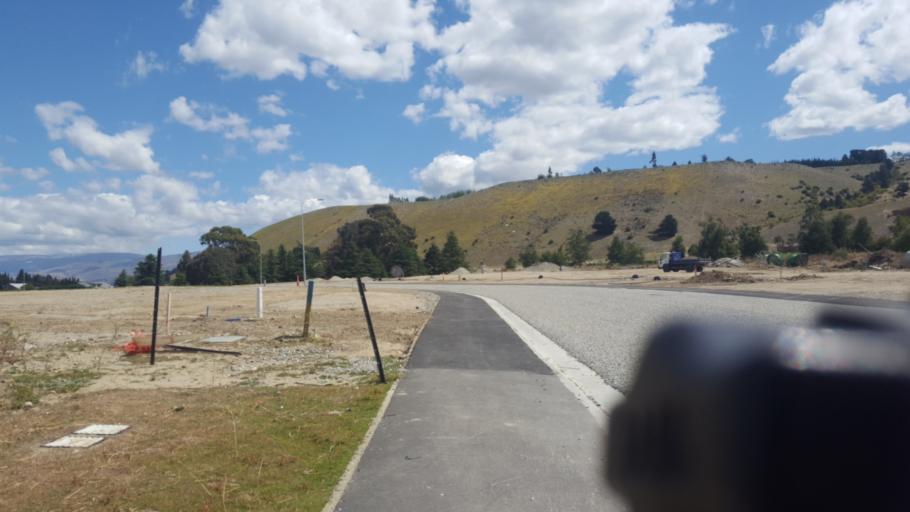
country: NZ
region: Otago
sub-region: Queenstown-Lakes District
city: Wanaka
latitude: -44.9761
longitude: 169.2382
